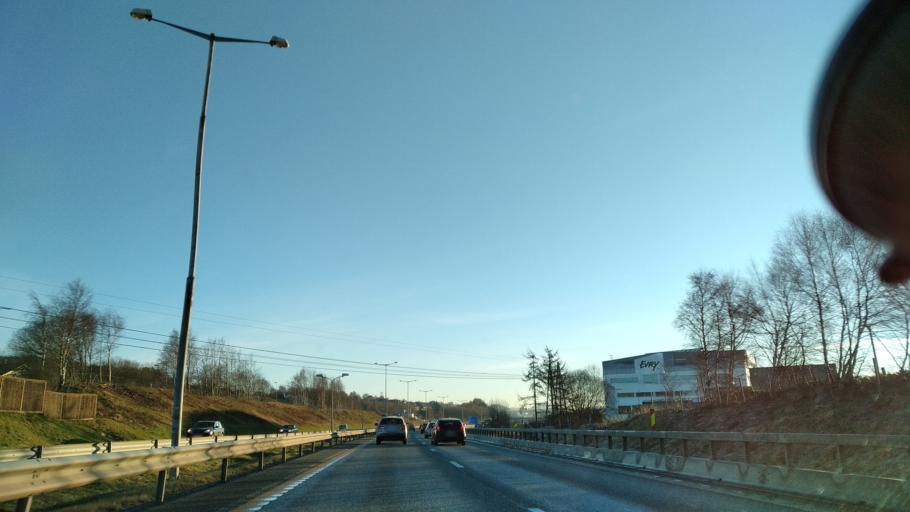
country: NO
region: Rogaland
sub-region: Sola
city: Sola
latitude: 58.9019
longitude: 5.7064
